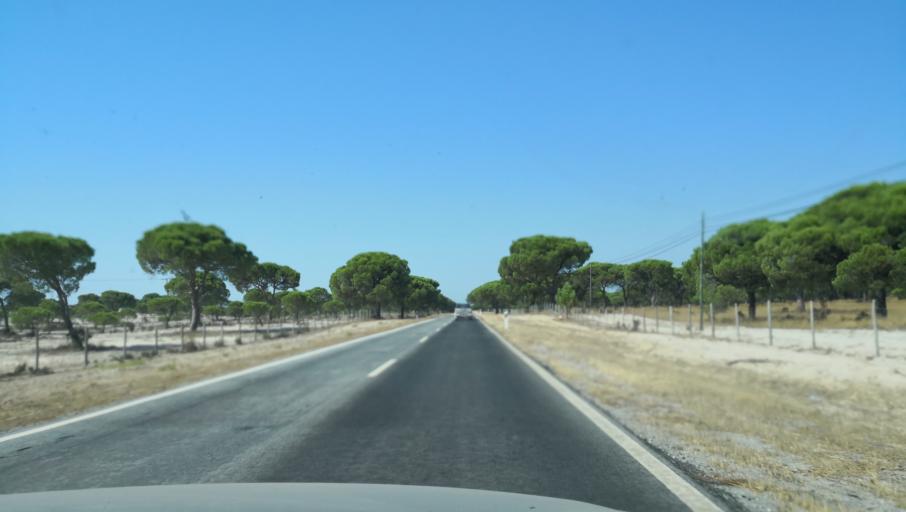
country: PT
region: Setubal
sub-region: Alcacer do Sal
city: Alcacer do Sal
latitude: 38.3823
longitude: -8.5608
